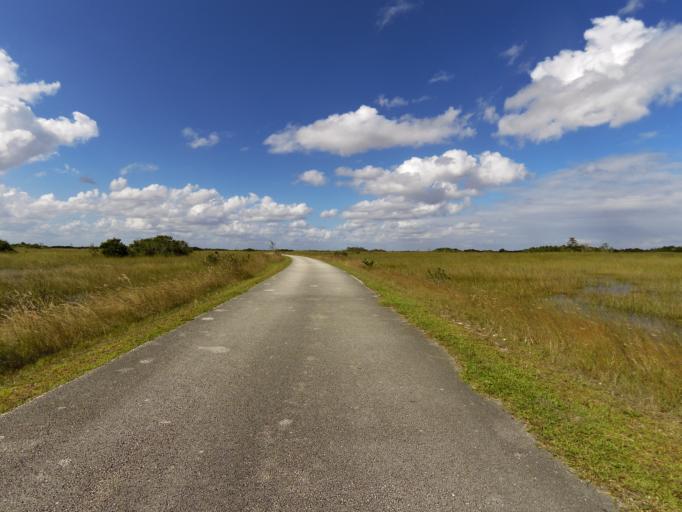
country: US
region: Florida
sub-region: Miami-Dade County
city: The Hammocks
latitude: 25.7271
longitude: -80.7587
